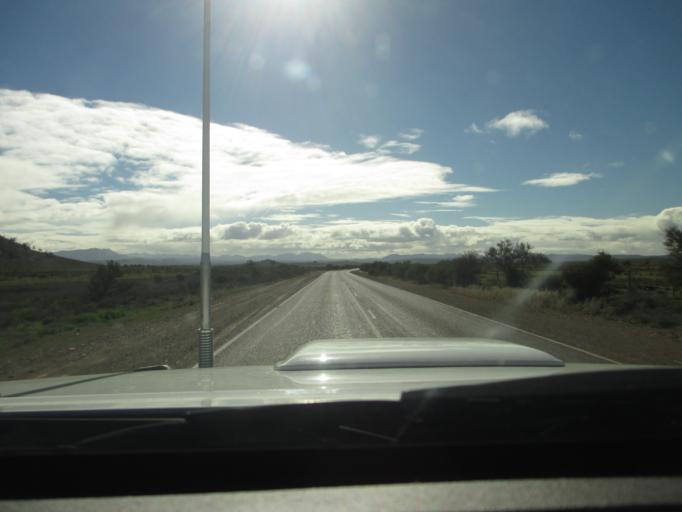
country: AU
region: South Australia
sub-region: Flinders Ranges
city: Quorn
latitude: -31.9164
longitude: 138.4278
